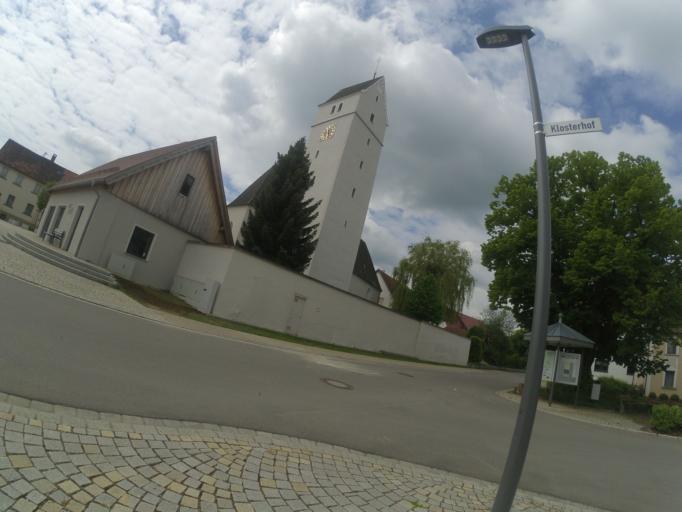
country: DE
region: Baden-Wuerttemberg
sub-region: Tuebingen Region
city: Berghulen
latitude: 48.4645
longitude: 9.7604
